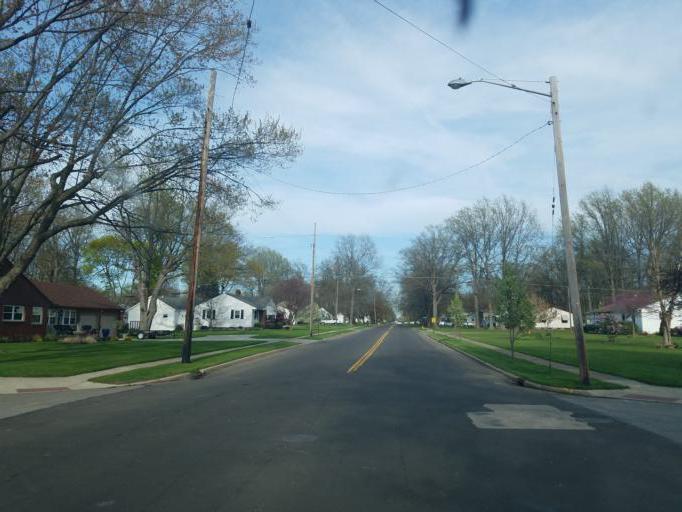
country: US
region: Ohio
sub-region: Ashtabula County
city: Ashtabula
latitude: 41.8925
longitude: -80.8226
